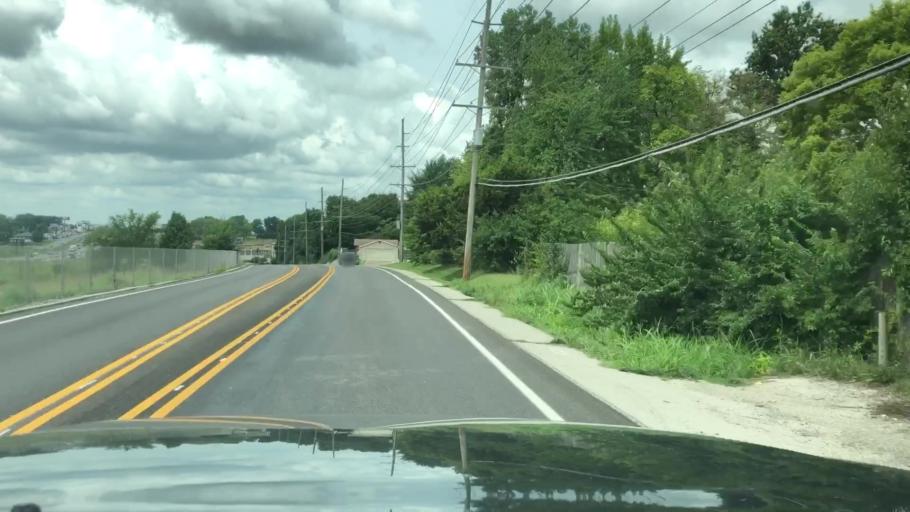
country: US
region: Missouri
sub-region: Saint Charles County
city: Saint Charles
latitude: 38.7891
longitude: -90.5433
